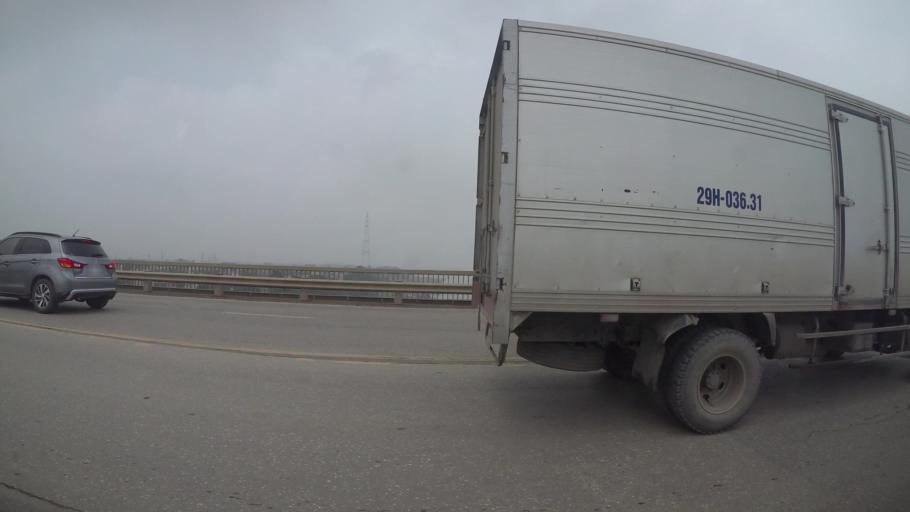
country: VN
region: Ha Noi
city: Tay Ho
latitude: 21.0948
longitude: 105.7862
